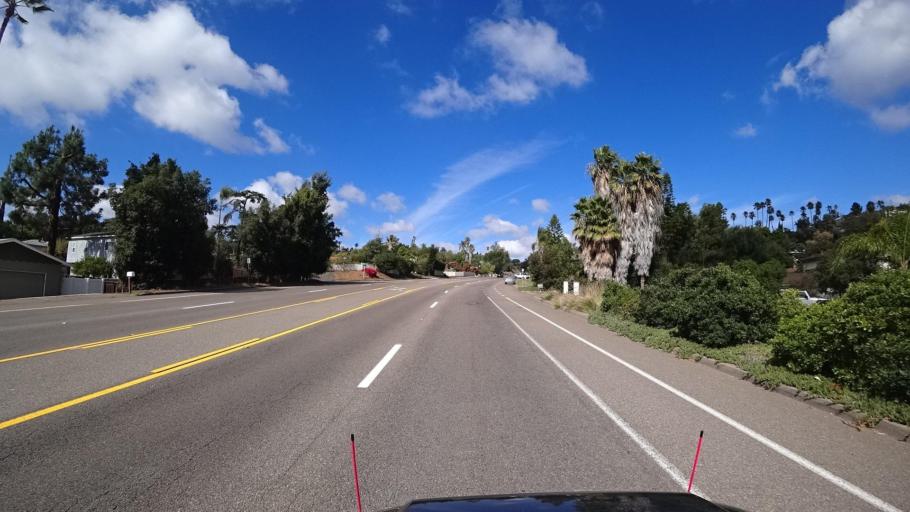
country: US
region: California
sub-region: San Diego County
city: Casa de Oro-Mount Helix
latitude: 32.7569
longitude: -116.9618
